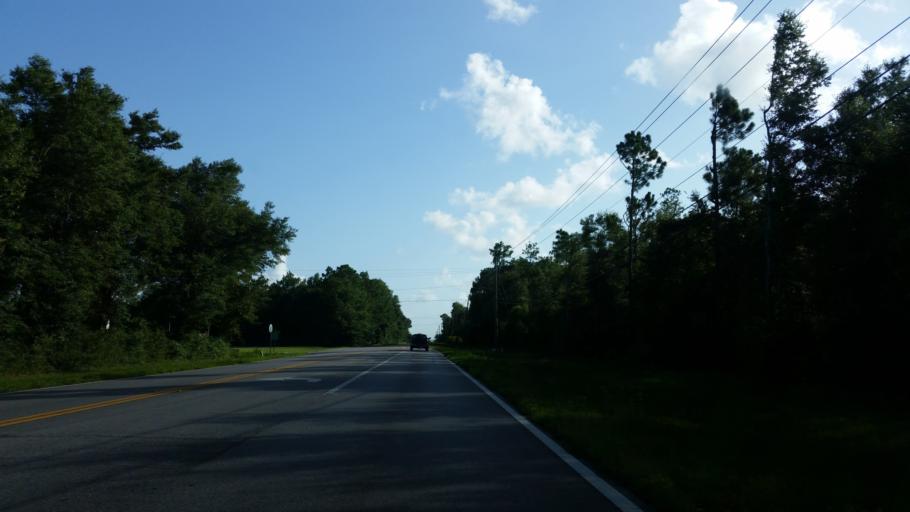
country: US
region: Florida
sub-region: Santa Rosa County
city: Pace
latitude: 30.5727
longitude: -87.0987
